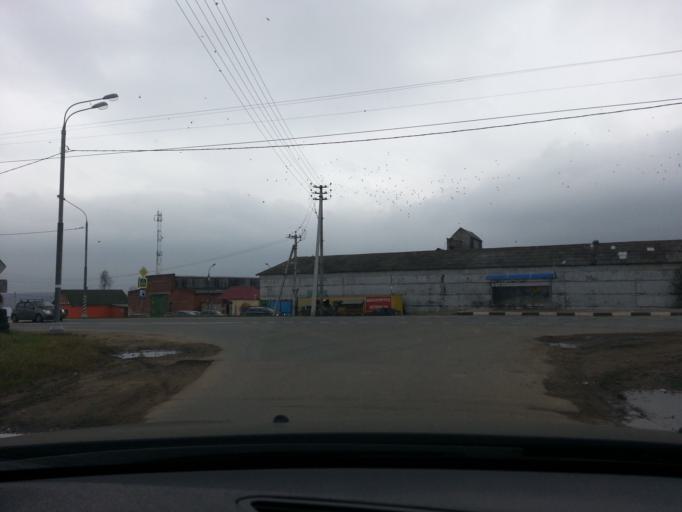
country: RU
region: Moskovskaya
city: Svatkovo
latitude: 56.3436
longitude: 38.2527
